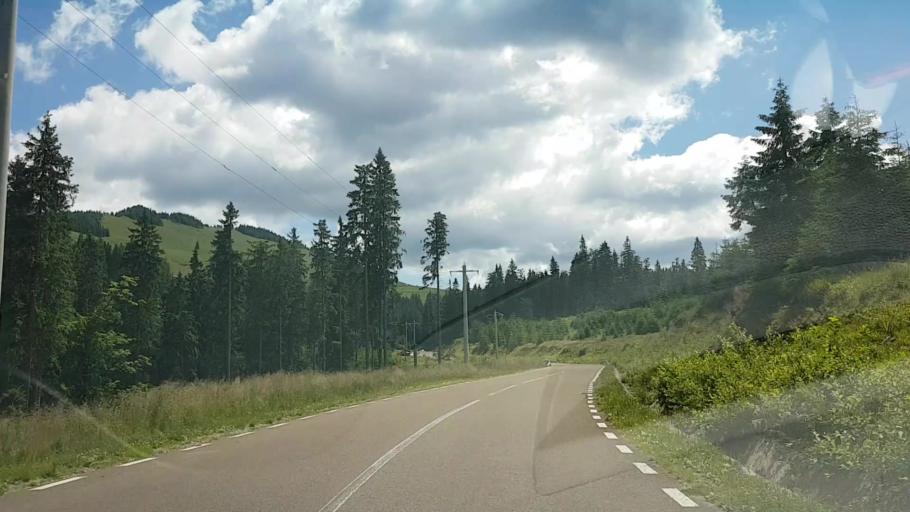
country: RO
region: Suceava
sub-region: Comuna Sadova
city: Sadova
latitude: 47.4588
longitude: 25.5171
